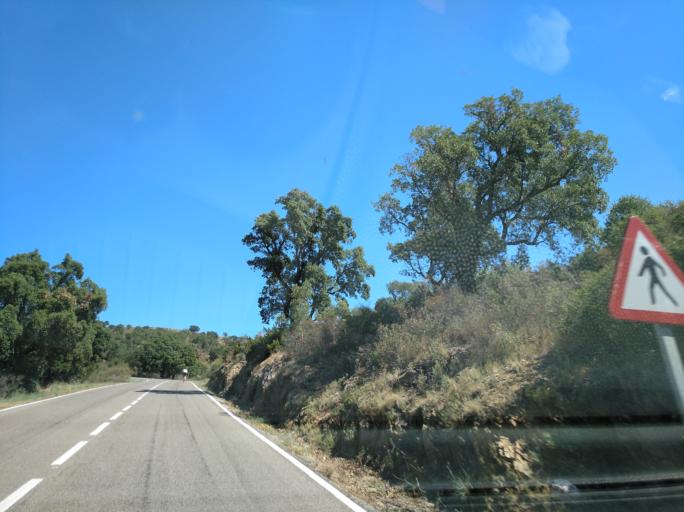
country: ES
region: Catalonia
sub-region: Provincia de Girona
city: Pau
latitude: 42.3342
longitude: 3.1182
